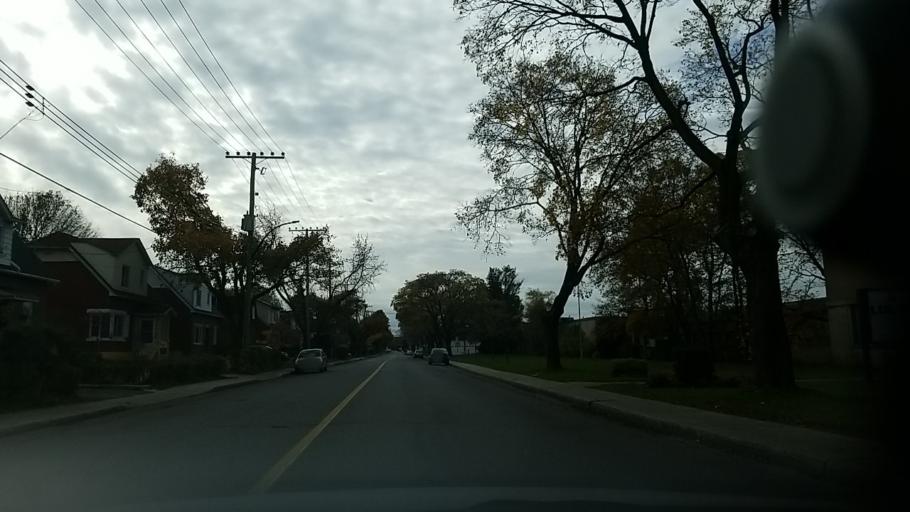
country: CA
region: Quebec
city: Saint-Laurent
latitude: 45.5133
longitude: -73.6650
